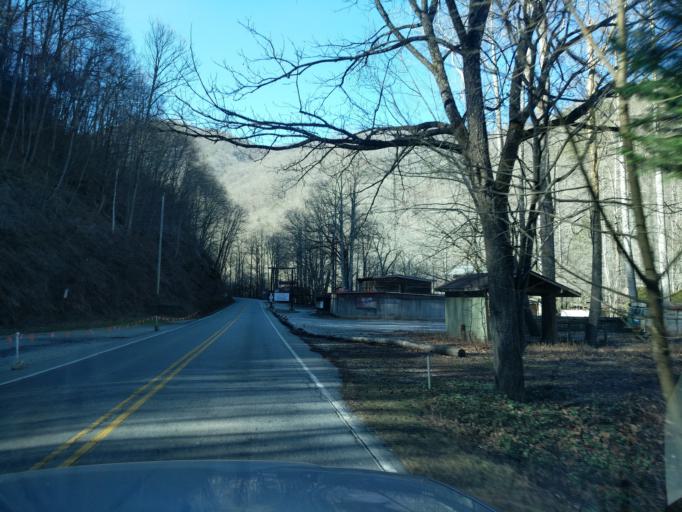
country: US
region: North Carolina
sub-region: Swain County
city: Bryson City
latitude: 35.3349
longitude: -83.6153
